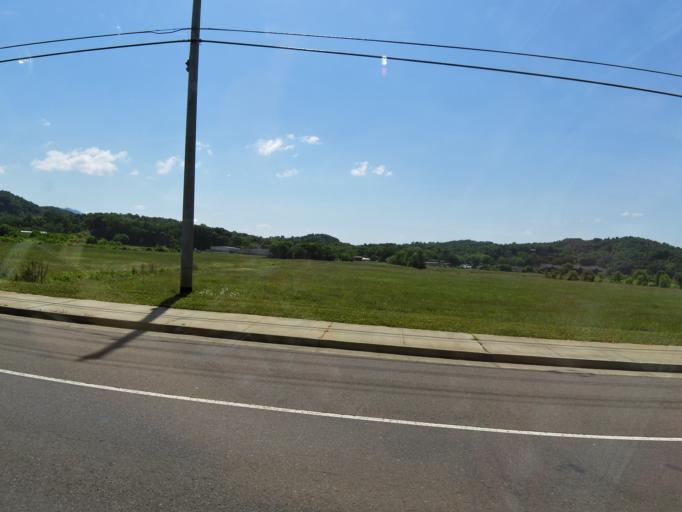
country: US
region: Tennessee
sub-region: Sevier County
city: Sevierville
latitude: 35.8832
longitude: -83.5730
